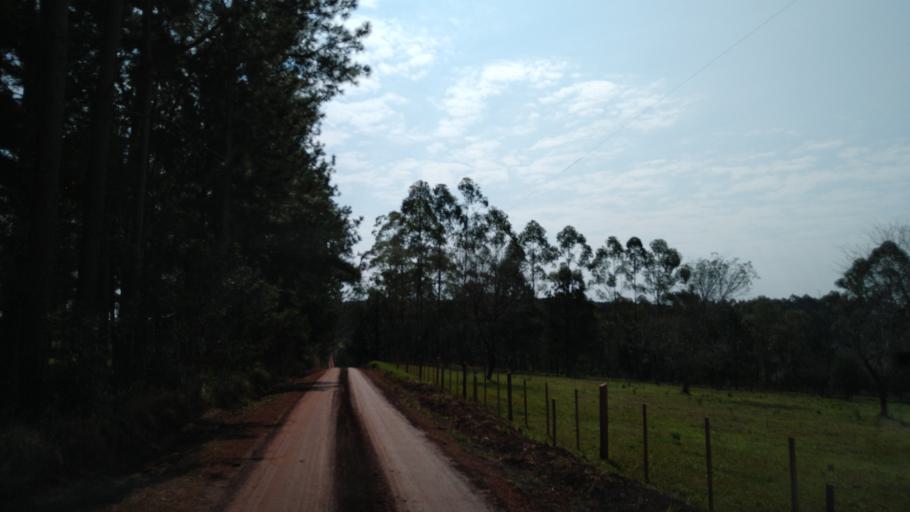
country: AR
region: Misiones
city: Capiovi
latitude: -26.9493
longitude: -55.0441
